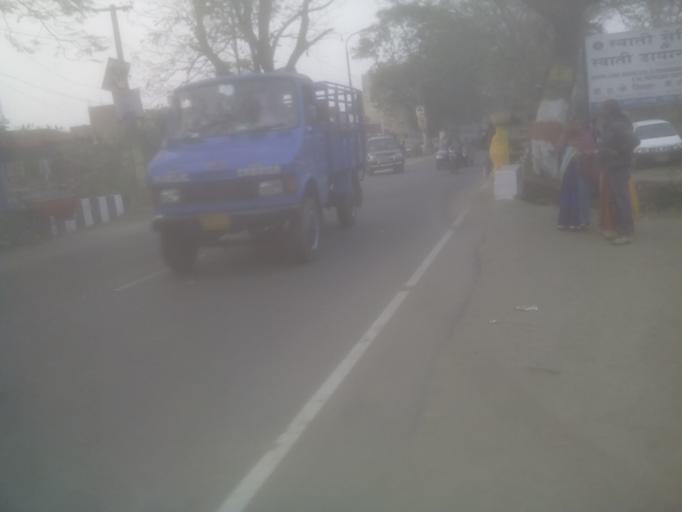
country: IN
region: Jharkhand
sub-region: Dhanbad
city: Dhanbad
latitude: 23.8114
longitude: 86.4326
